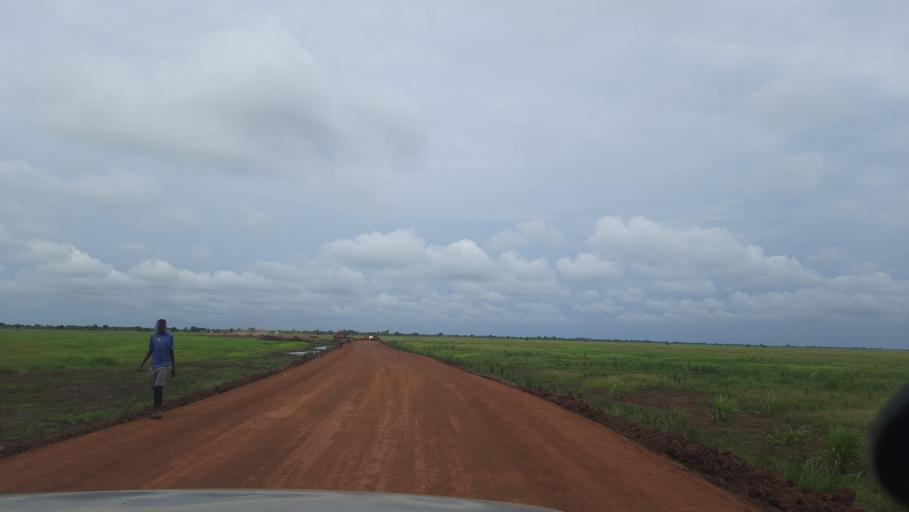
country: ET
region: Gambela
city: Gambela
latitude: 8.3407
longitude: 33.7783
